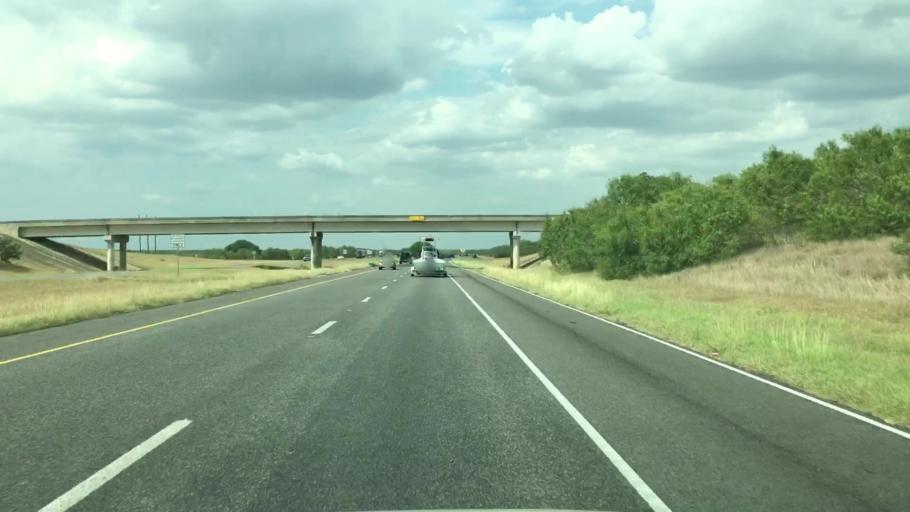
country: US
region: Texas
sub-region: Atascosa County
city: Pleasanton
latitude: 28.9152
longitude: -98.4346
